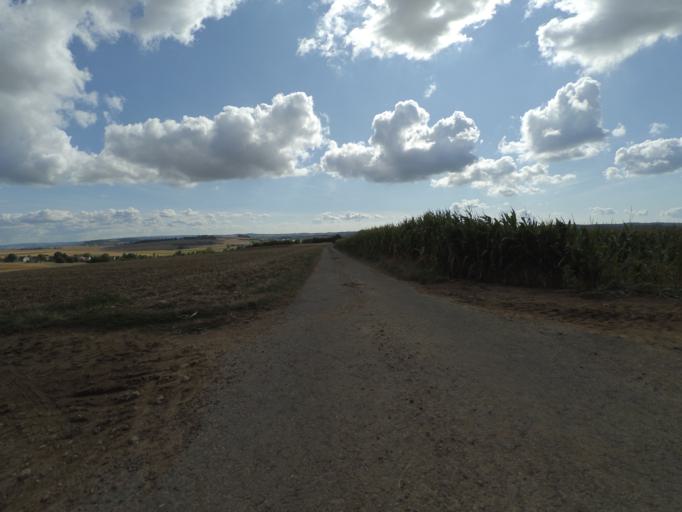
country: DE
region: Rheinland-Pfalz
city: Kirf
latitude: 49.5292
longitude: 6.4556
